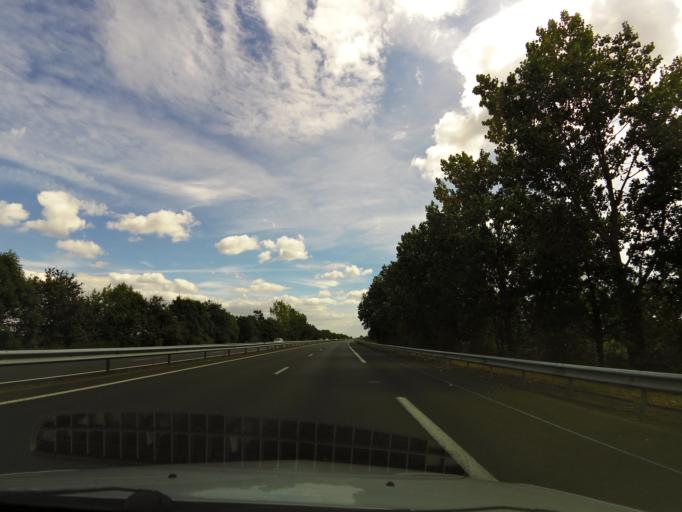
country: FR
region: Pays de la Loire
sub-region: Departement de la Vendee
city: Les Brouzils
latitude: 46.8957
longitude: -1.3005
